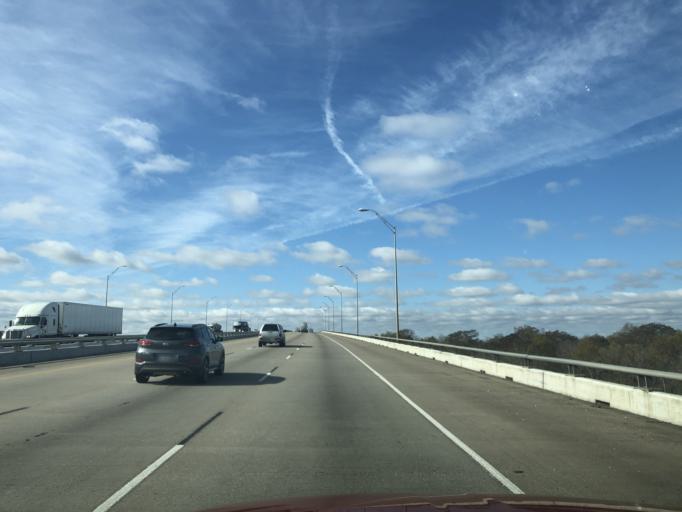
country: US
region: Texas
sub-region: Chambers County
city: Old River-Winfree
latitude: 29.8387
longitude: -94.7583
